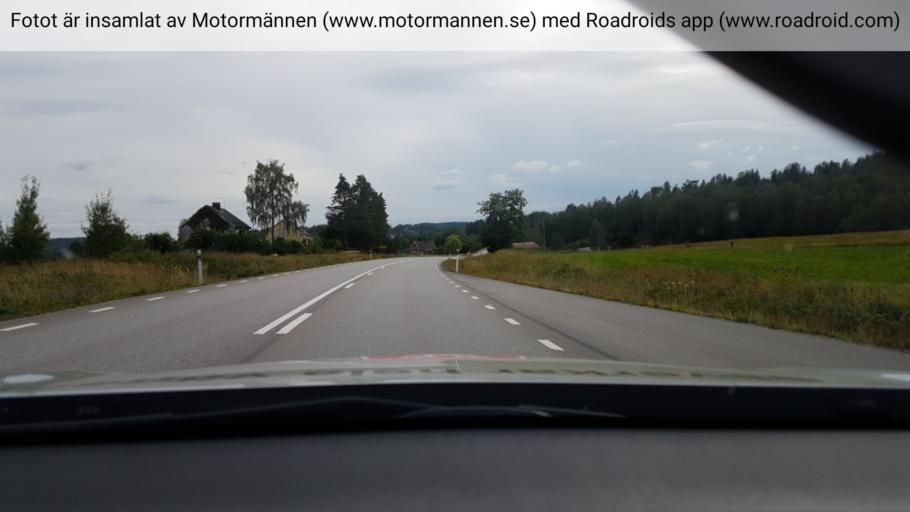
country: SE
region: Vaestra Goetaland
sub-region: Bengtsfors Kommun
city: Billingsfors
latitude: 59.0323
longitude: 12.3105
